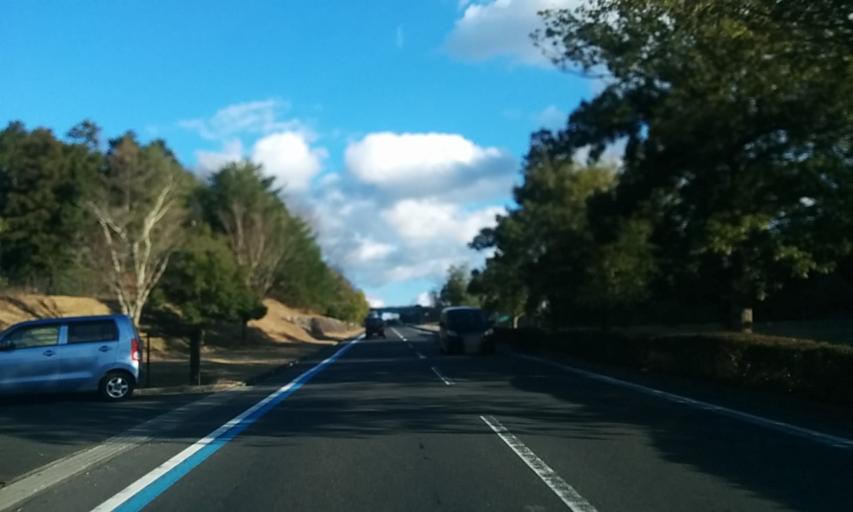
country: JP
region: Kyoto
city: Fukuchiyama
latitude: 35.3163
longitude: 135.1316
